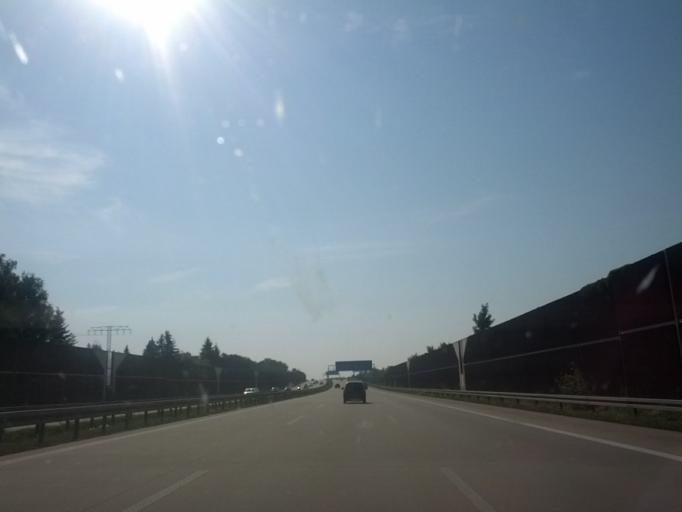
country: DE
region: Brandenburg
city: Neuenhagen
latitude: 52.5129
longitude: 13.7300
